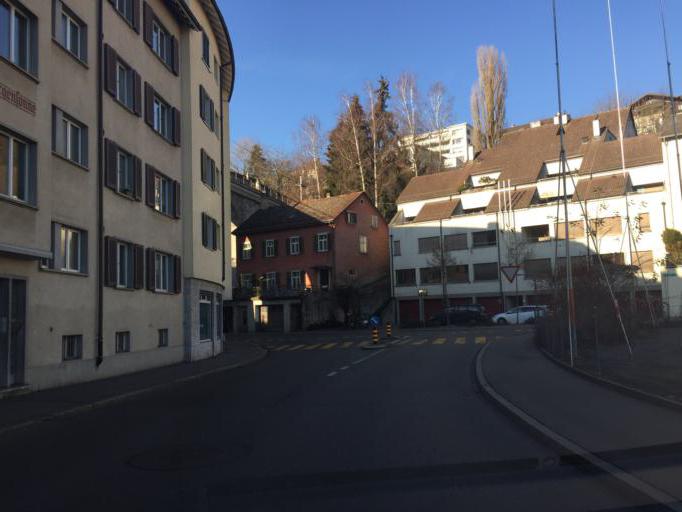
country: CH
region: Zurich
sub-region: Bezirk Andelfingen
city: Feuerthalen
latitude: 47.6953
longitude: 8.6440
